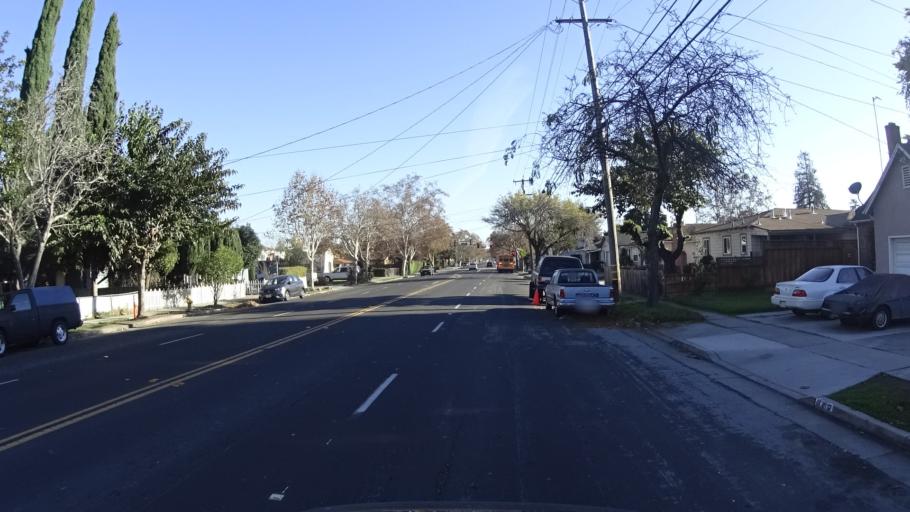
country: US
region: California
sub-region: Santa Clara County
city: San Jose
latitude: 37.3559
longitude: -121.9011
